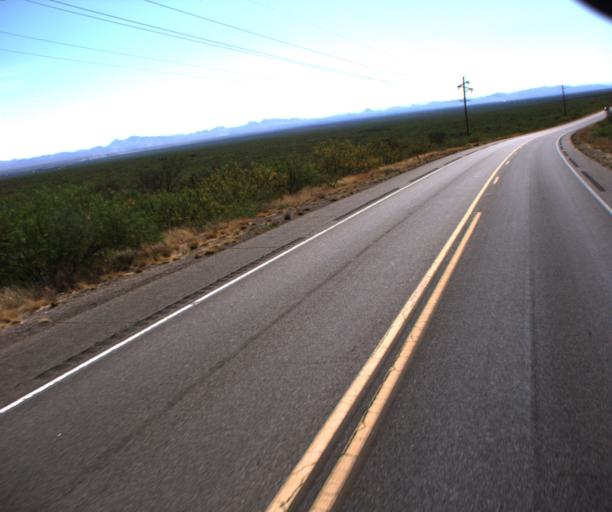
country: US
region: Arizona
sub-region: Cochise County
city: Bisbee
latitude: 31.4397
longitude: -109.8213
